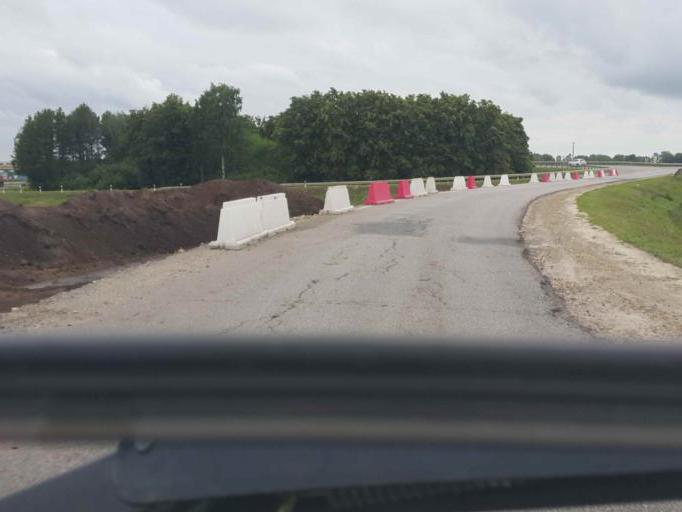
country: RU
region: Tambov
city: Zavoronezhskoye
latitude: 52.9086
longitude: 40.6366
